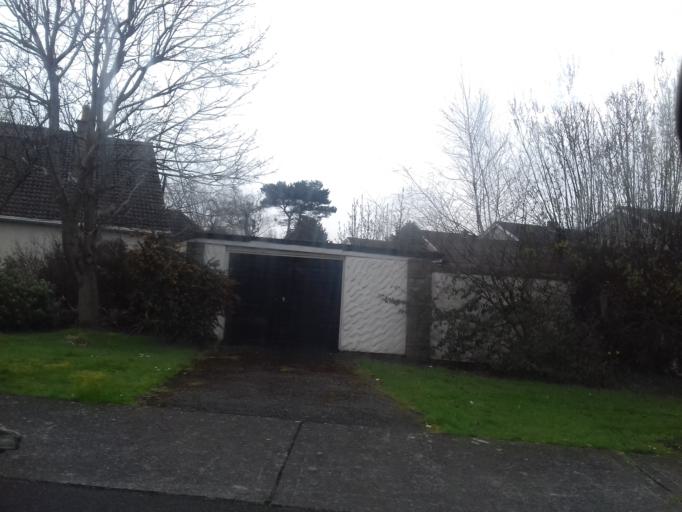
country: IE
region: Leinster
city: Portmarnock
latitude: 53.4233
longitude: -6.1326
